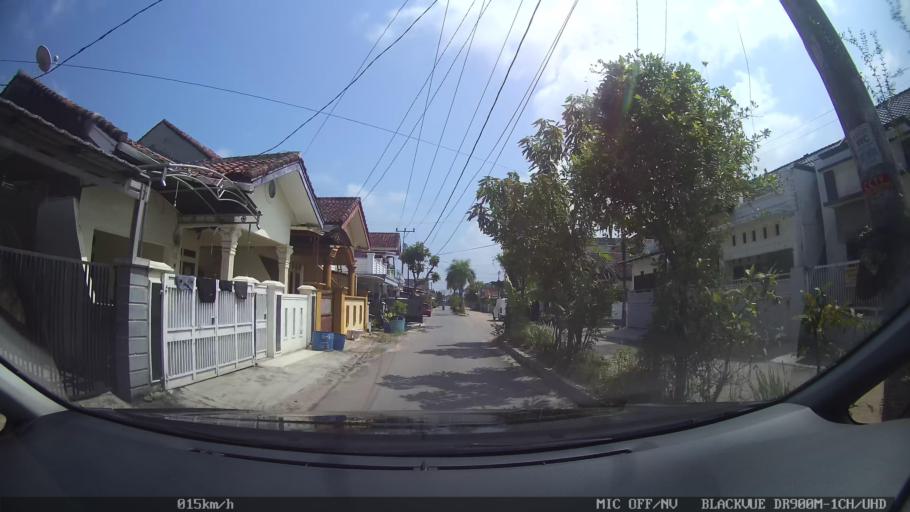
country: ID
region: Lampung
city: Kedaton
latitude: -5.3592
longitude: 105.2809
